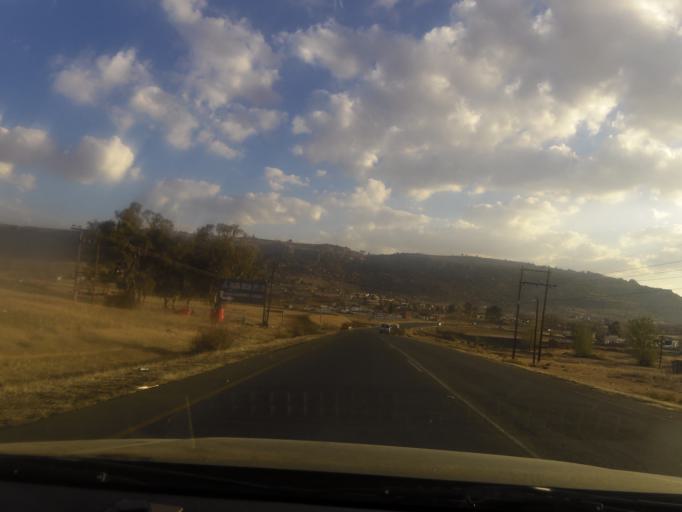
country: LS
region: Maseru
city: Maseru
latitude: -29.2662
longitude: 27.5990
